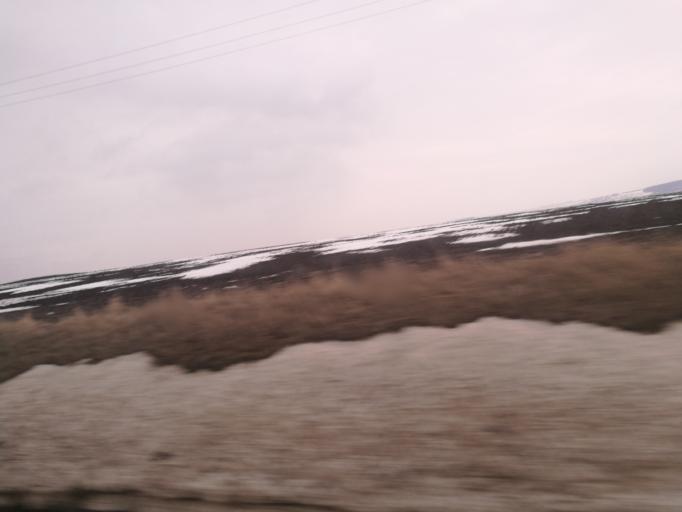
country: RO
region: Iasi
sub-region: Comuna Targu Frumos
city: Targu Frumos
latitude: 47.2056
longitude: 26.9856
